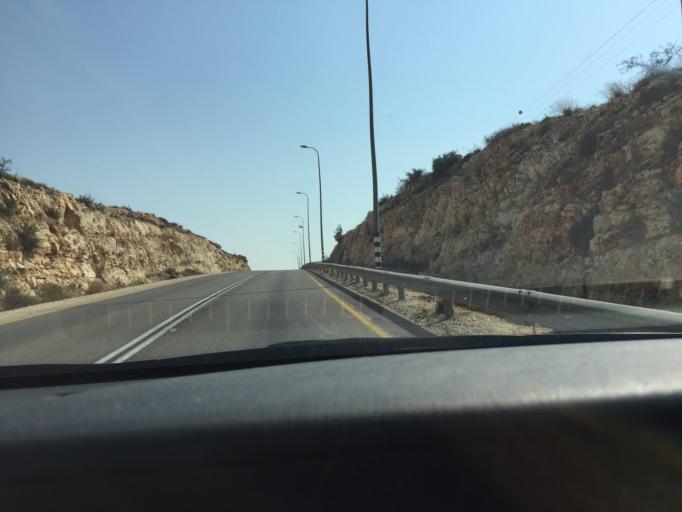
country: PS
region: West Bank
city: Bruqin
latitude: 32.0852
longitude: 35.1037
